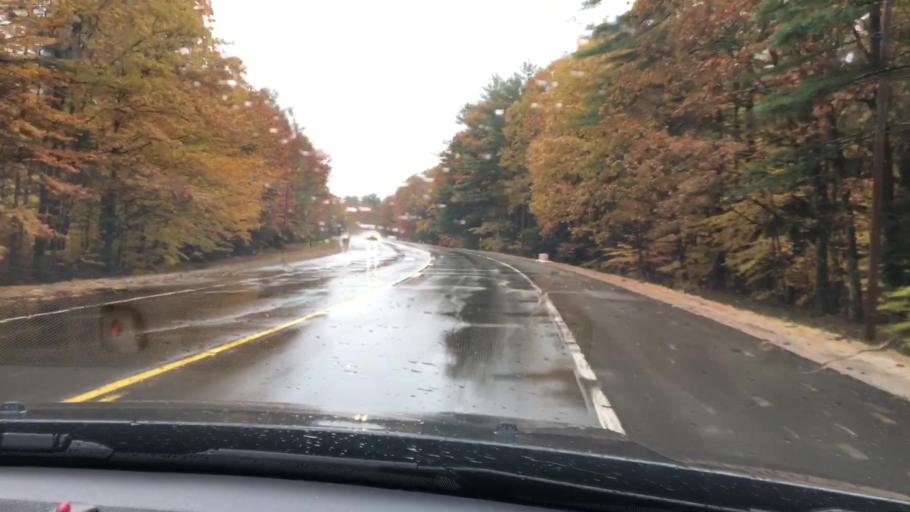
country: US
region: New Hampshire
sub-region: Grafton County
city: Ashland
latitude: 43.7167
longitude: -71.6246
